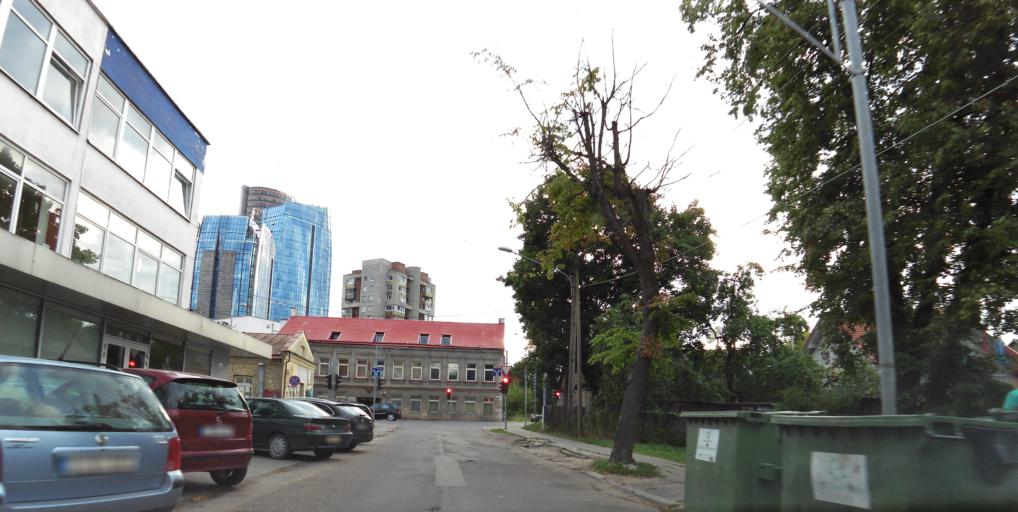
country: LT
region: Vilnius County
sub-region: Vilnius
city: Vilnius
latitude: 54.6969
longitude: 25.2826
